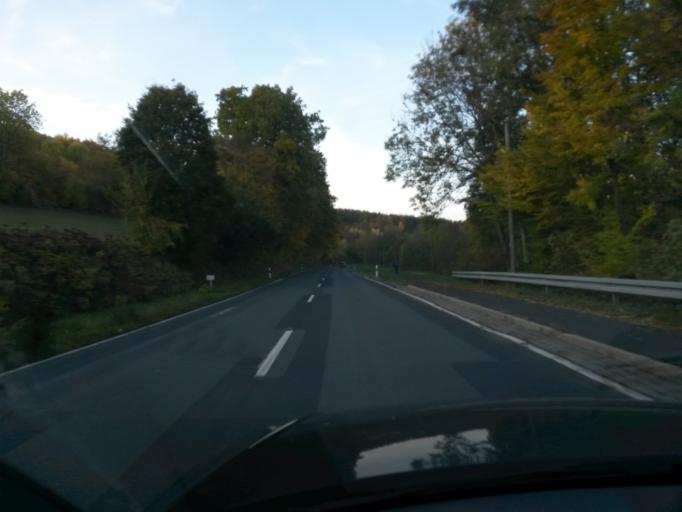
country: DE
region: Bavaria
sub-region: Regierungsbezirk Unterfranken
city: Rimpar
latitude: 49.8310
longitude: 9.9567
